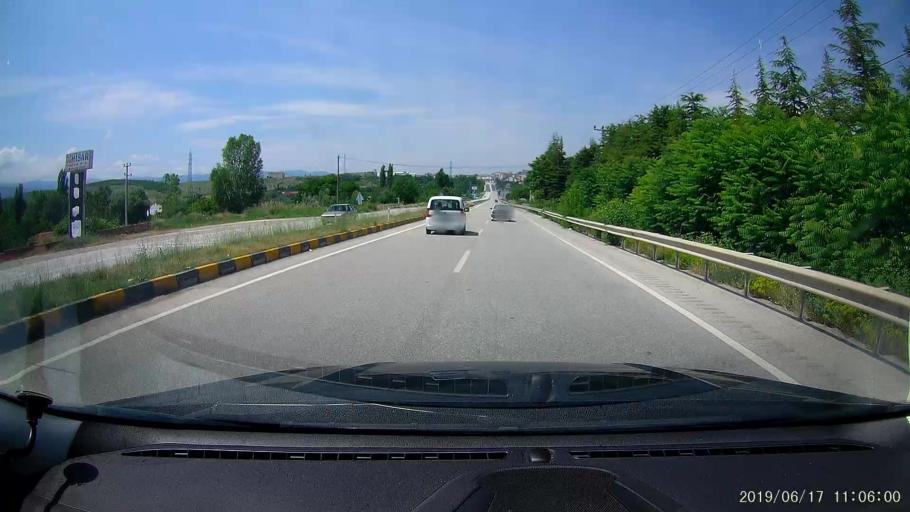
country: TR
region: Kastamonu
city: Tosya
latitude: 41.0168
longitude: 34.0737
